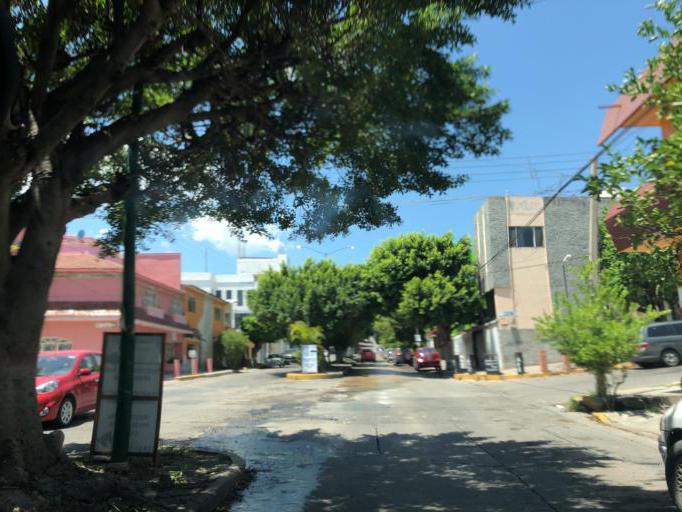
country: MX
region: Chiapas
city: Tuxtla Gutierrez
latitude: 16.7522
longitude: -93.1263
